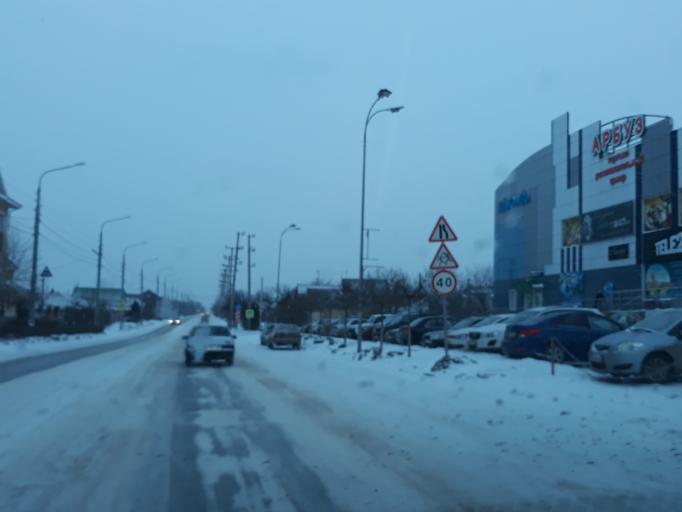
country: RU
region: Rostov
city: Taganrog
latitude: 47.2762
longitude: 38.9156
